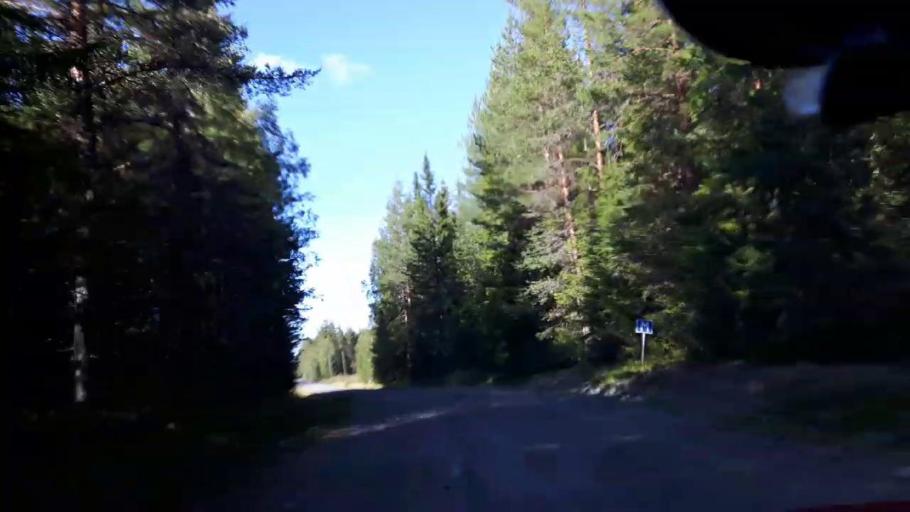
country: SE
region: Jaemtland
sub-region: Ragunda Kommun
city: Hammarstrand
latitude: 63.5156
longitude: 16.0567
